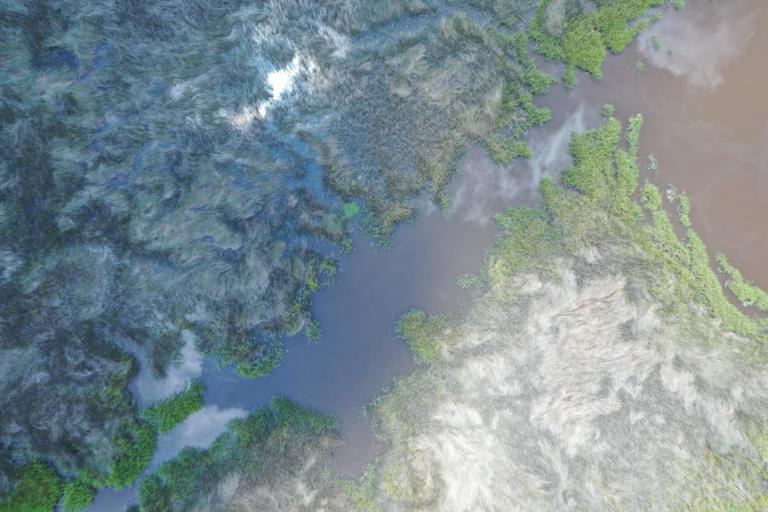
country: US
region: Georgia
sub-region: Chatham County
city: Georgetown
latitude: 32.0267
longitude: -81.2057
